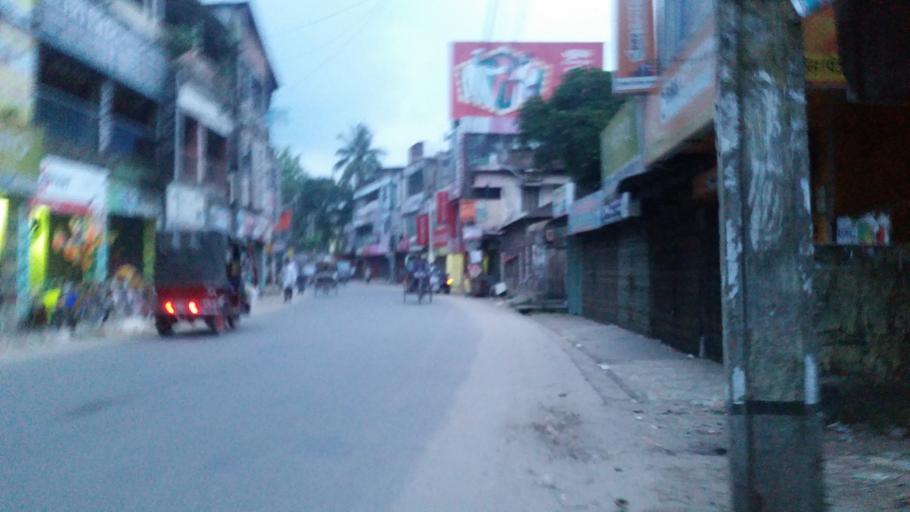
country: BD
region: Dhaka
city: Tangail
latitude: 24.2518
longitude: 89.9185
